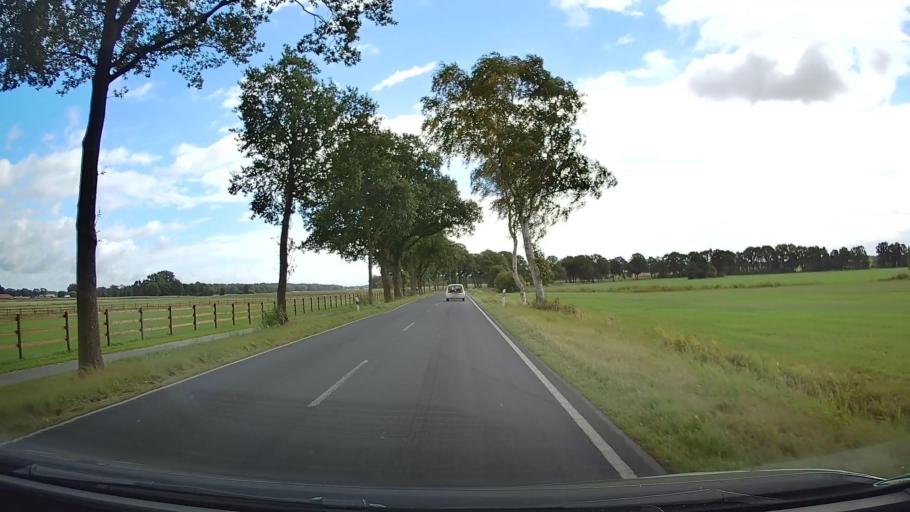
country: DE
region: Lower Saxony
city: Rhade
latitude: 53.3255
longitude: 9.1210
